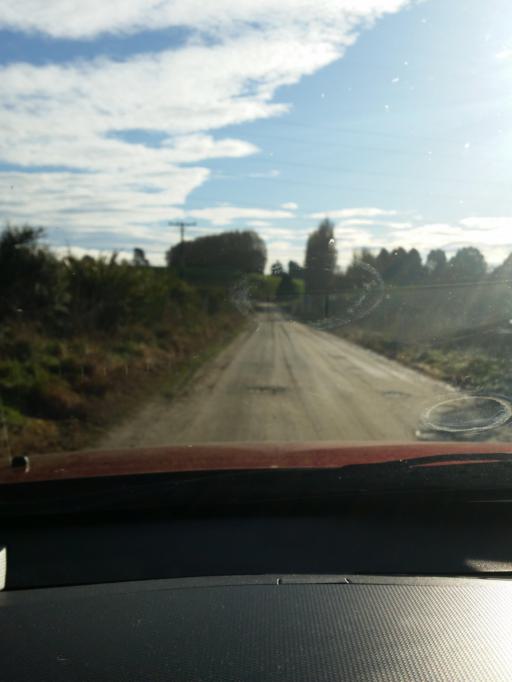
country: NZ
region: Southland
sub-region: Gore District
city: Gore
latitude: -46.2058
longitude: 168.7684
